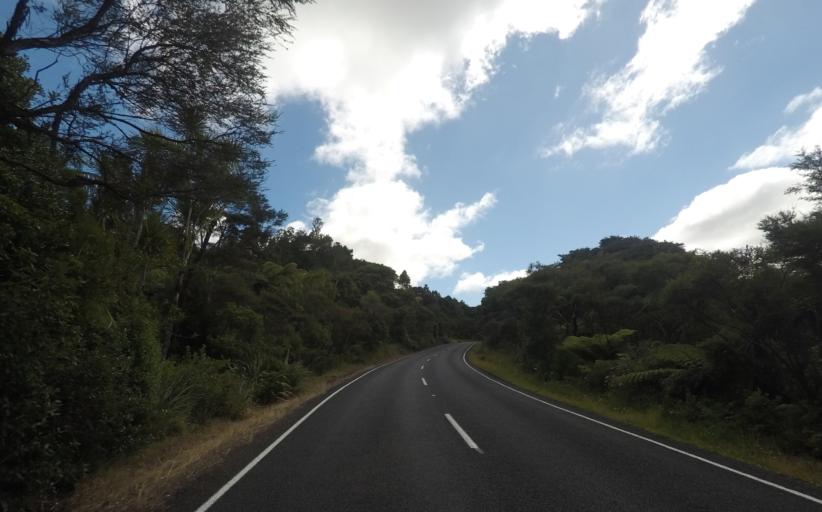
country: NZ
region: Auckland
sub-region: Auckland
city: Muriwai Beach
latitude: -36.8627
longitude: 174.5159
